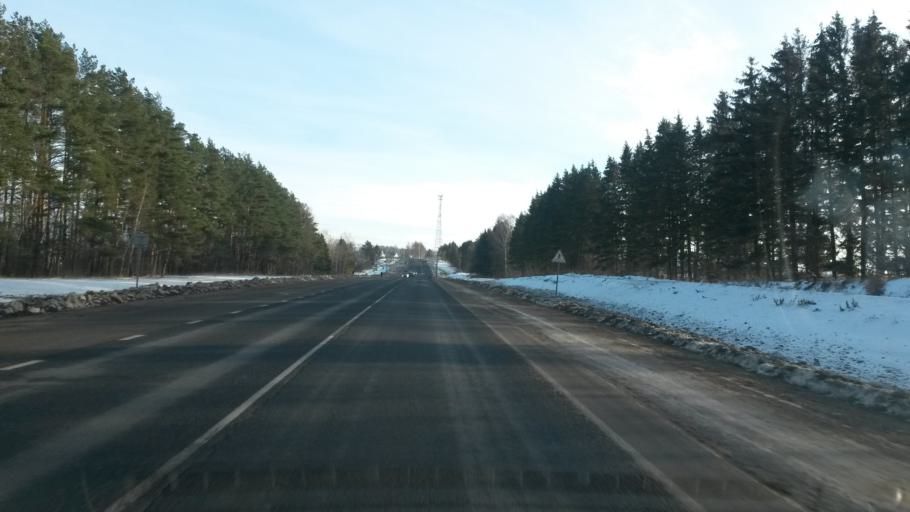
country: RU
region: Jaroslavl
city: Levashevo
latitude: 57.6437
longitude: 40.5138
